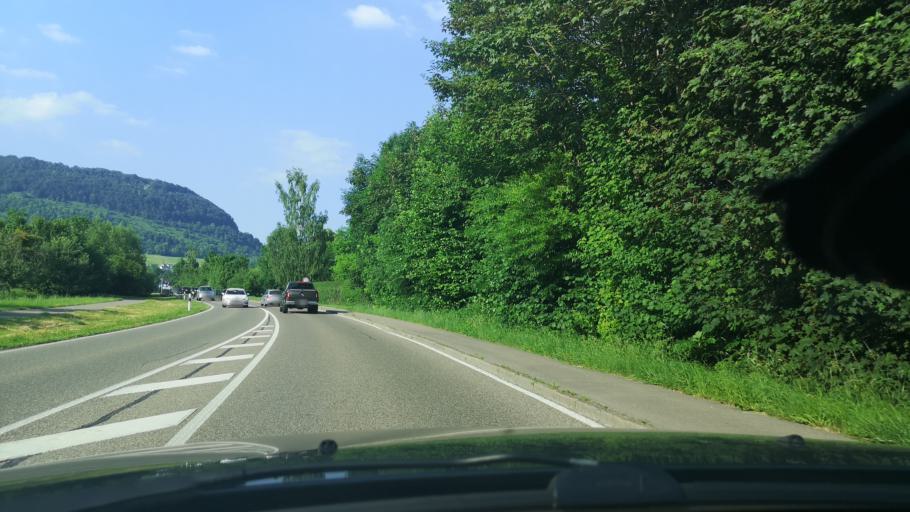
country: DE
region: Baden-Wuerttemberg
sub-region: Regierungsbezirk Stuttgart
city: Bad Ditzenbach
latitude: 48.5893
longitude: 9.7055
